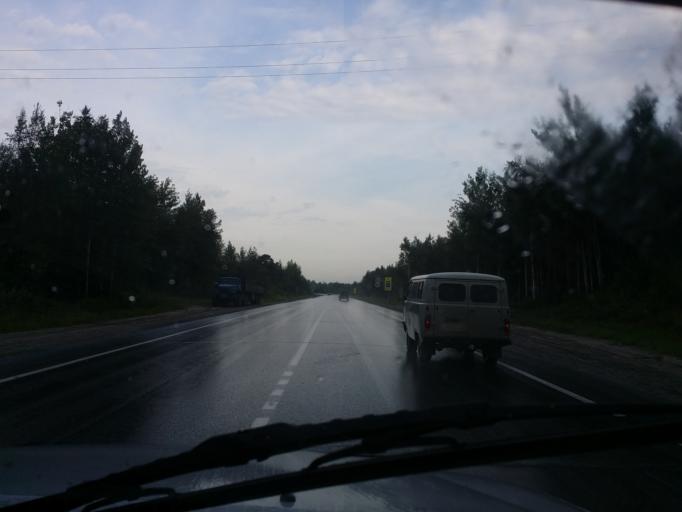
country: RU
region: Khanty-Mansiyskiy Avtonomnyy Okrug
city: Megion
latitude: 61.1068
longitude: 76.0418
